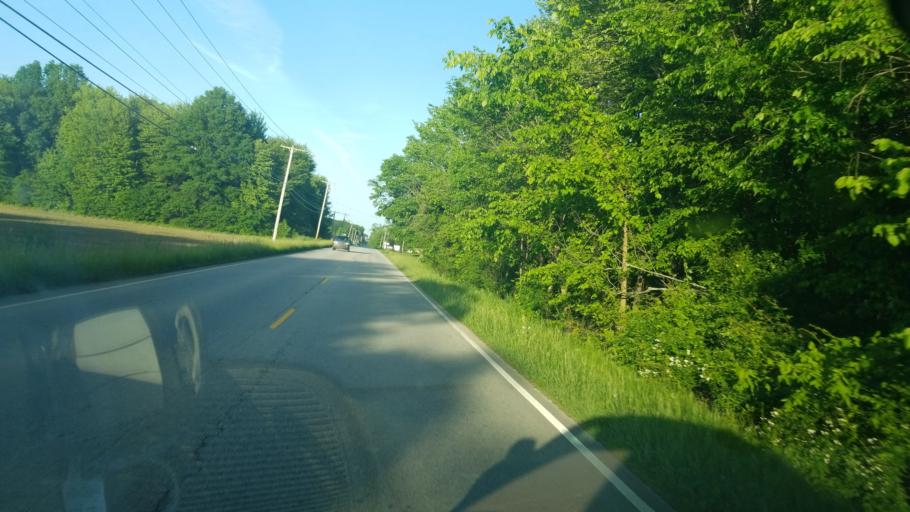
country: US
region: Ohio
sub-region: Mahoning County
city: Craig Beach
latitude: 41.0993
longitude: -80.9440
